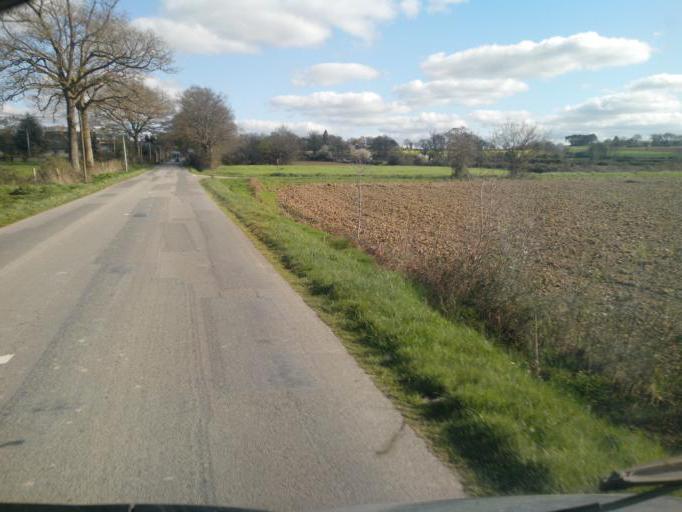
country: FR
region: Brittany
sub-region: Departement d'Ille-et-Vilaine
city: Messac
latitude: 47.7871
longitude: -1.7876
